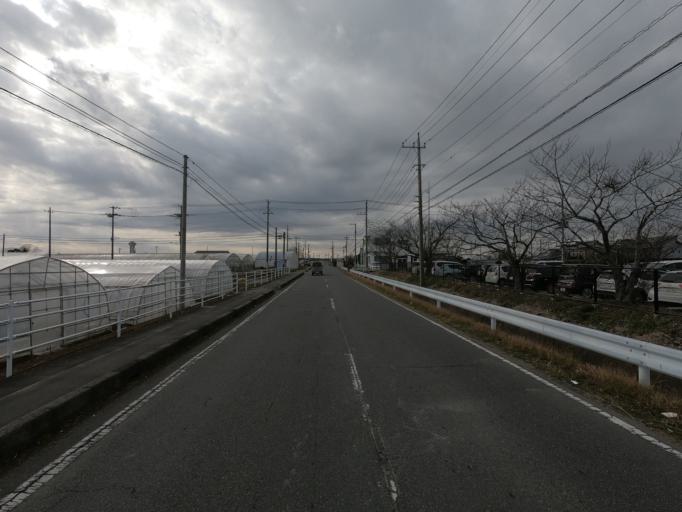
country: JP
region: Ibaraki
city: Ishioka
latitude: 36.1049
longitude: 140.4141
